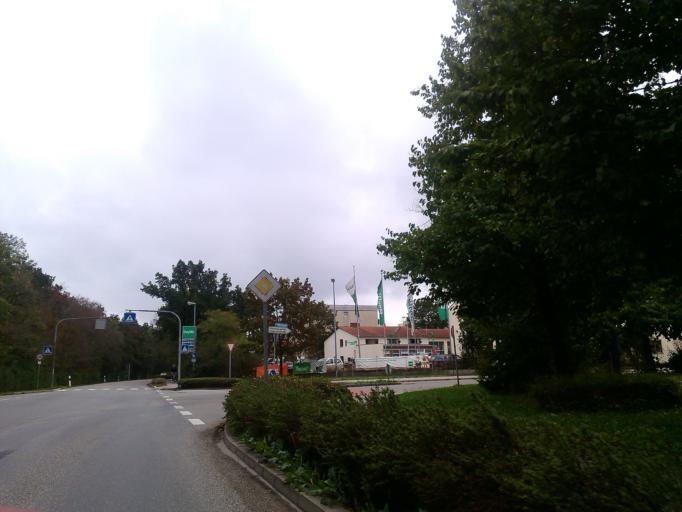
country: DE
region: Bavaria
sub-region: Upper Bavaria
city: Fuerstenfeldbruck
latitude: 48.1788
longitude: 11.2304
